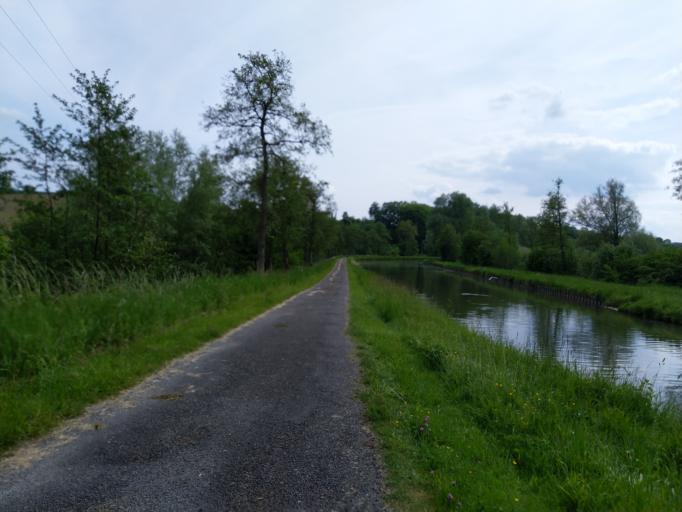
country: FR
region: Picardie
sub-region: Departement de l'Aisne
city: Etreux
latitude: 49.9604
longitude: 3.6173
